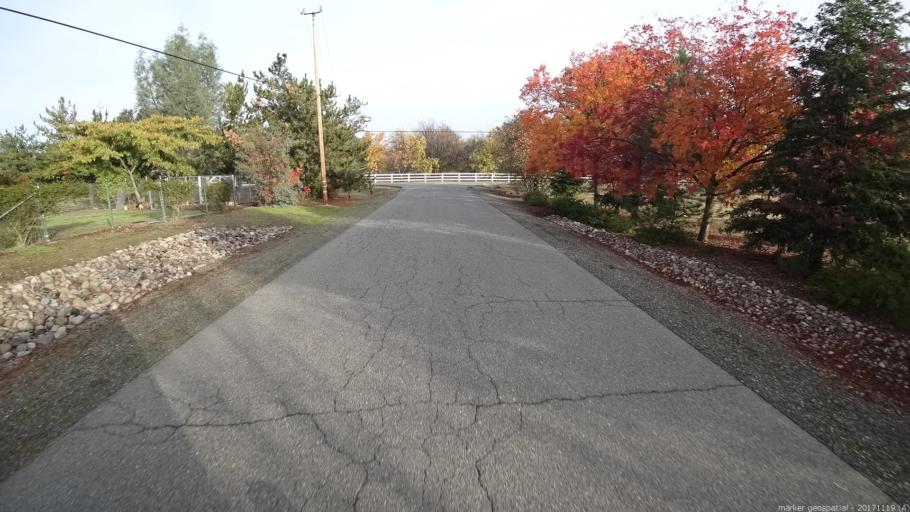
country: US
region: California
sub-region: Shasta County
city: Anderson
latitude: 40.5051
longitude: -122.3435
